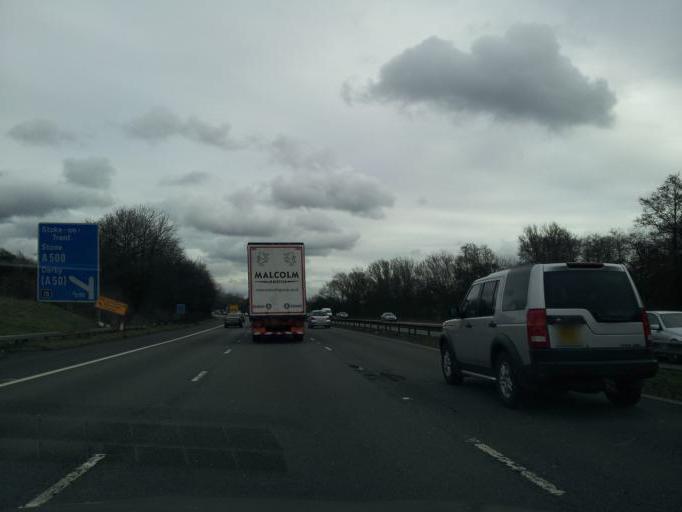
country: GB
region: England
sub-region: Staffordshire
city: Newcastle under Lyme
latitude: 52.9831
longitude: -2.2421
